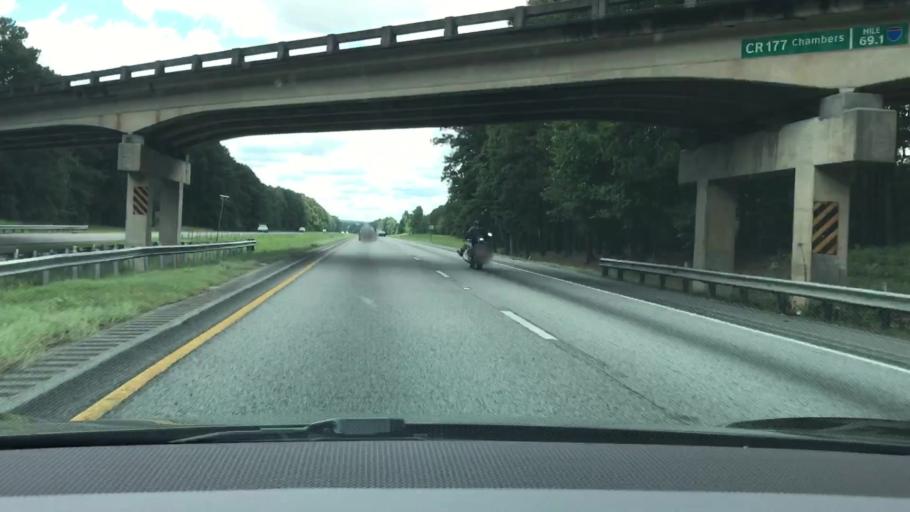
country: US
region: Alabama
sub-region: Lee County
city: Opelika
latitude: 32.7312
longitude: -85.2932
